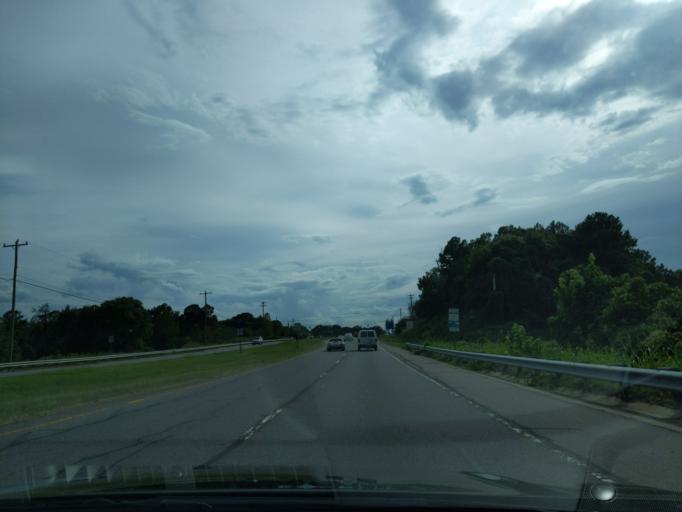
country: US
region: North Carolina
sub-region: Cabarrus County
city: Concord
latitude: 35.3629
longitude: -80.5875
